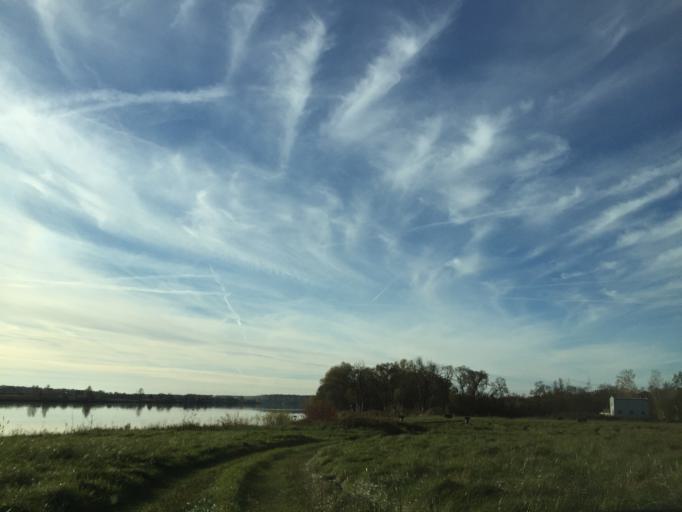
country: LV
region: Skriveri
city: Skriveri
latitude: 56.6217
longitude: 25.1272
